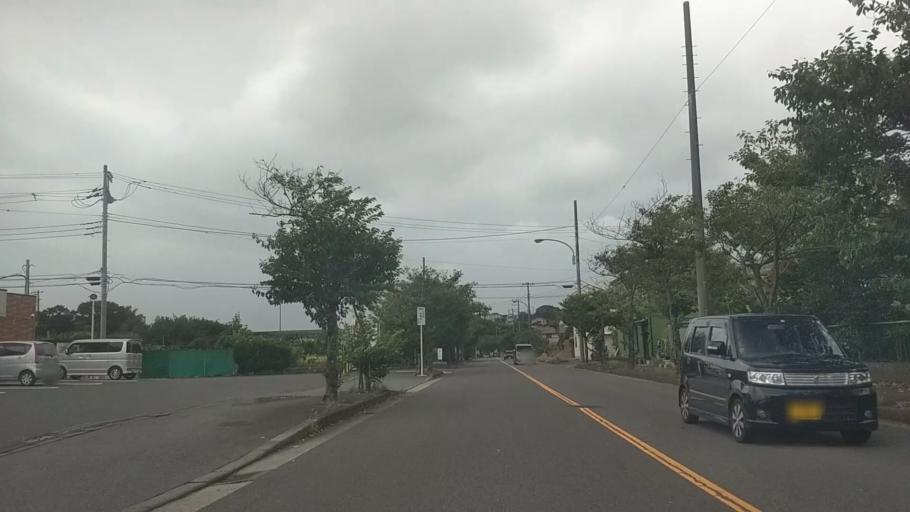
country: JP
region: Kanagawa
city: Hayama
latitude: 35.2350
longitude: 139.6176
